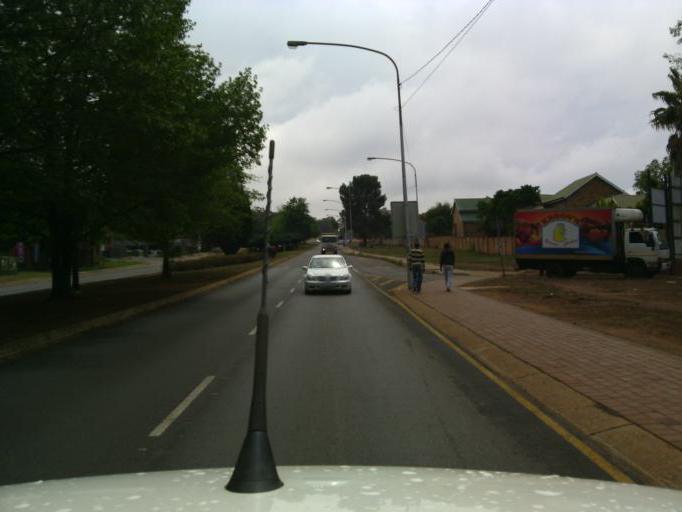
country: ZA
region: Gauteng
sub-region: City of Tshwane Metropolitan Municipality
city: Centurion
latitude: -25.8481
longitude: 28.1904
